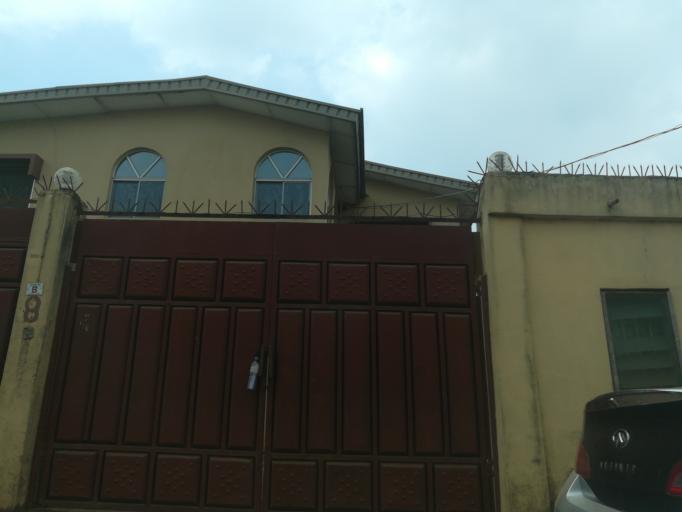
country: NG
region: Lagos
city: Ikorodu
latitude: 6.6185
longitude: 3.5200
